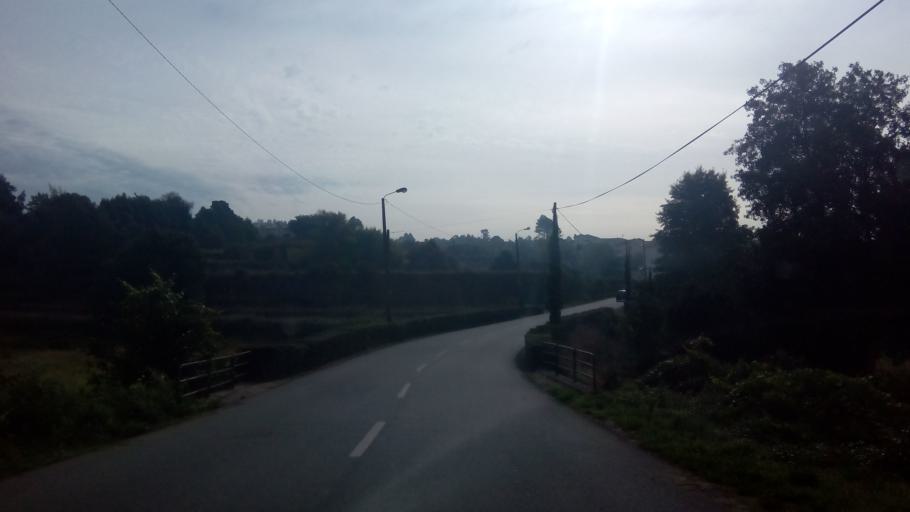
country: PT
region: Porto
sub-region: Paredes
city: Gandra
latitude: 41.1936
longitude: -8.4315
